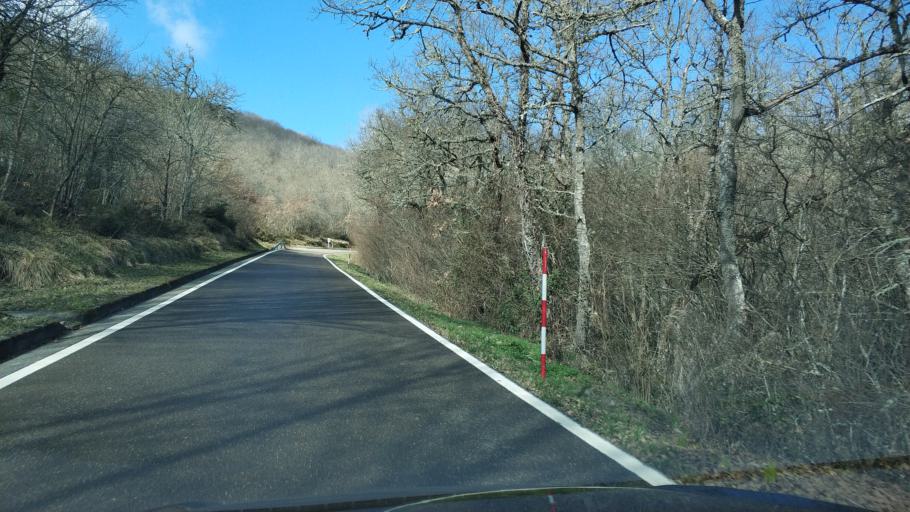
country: ES
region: Cantabria
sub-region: Provincia de Cantabria
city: Mataporquera
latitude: 42.9023
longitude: -4.0497
